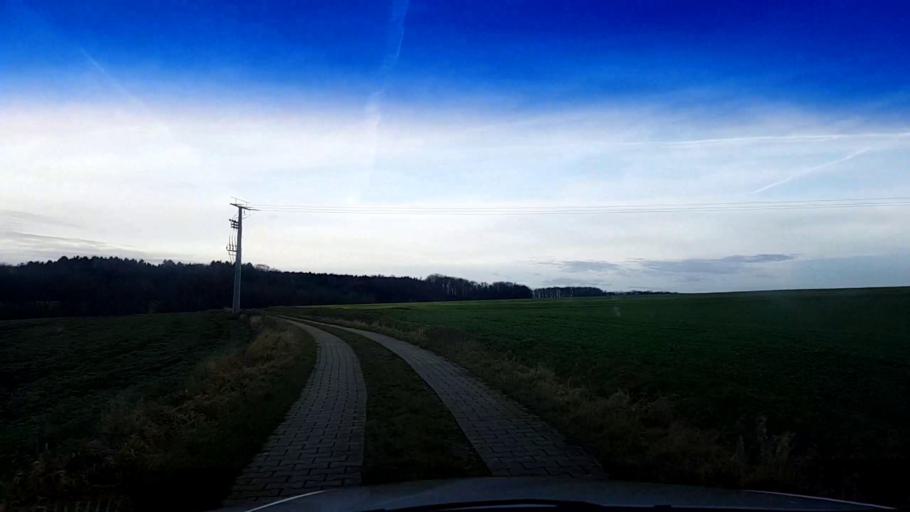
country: DE
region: Bavaria
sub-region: Upper Franconia
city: Schesslitz
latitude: 49.9896
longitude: 11.0383
